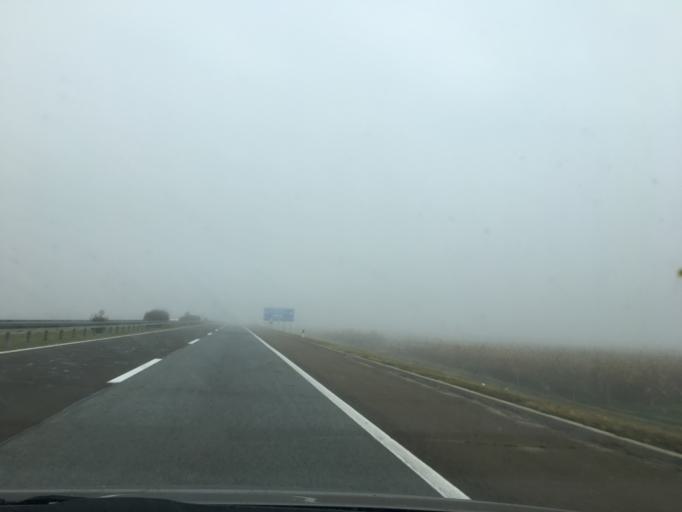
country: RS
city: Novi Karlovci
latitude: 45.0658
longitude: 20.1571
